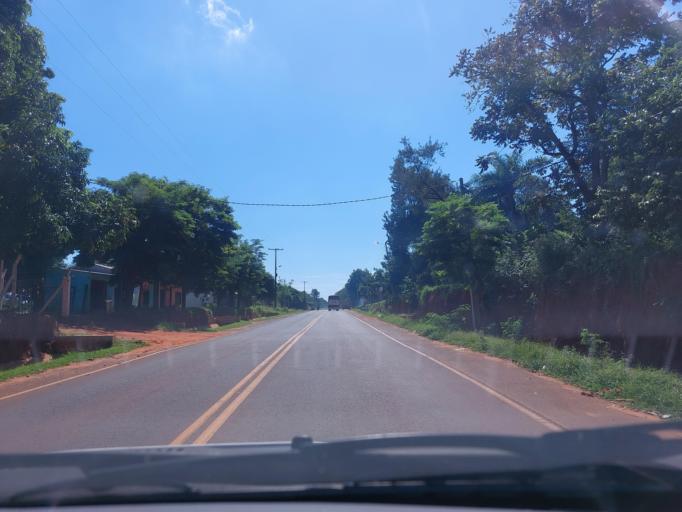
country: PY
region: San Pedro
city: Guayaybi
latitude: -24.5942
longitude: -56.5196
